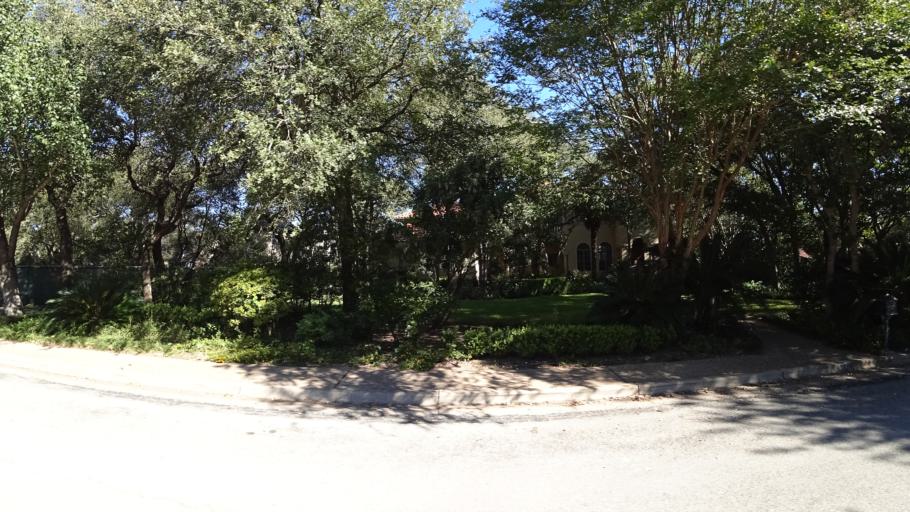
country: US
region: Texas
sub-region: Travis County
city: West Lake Hills
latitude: 30.3327
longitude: -97.7847
